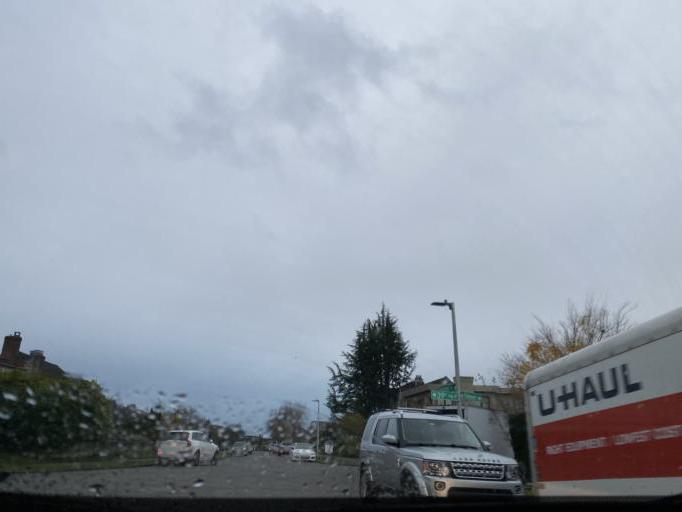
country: US
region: Washington
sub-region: King County
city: Seattle
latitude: 47.6423
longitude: -122.4076
